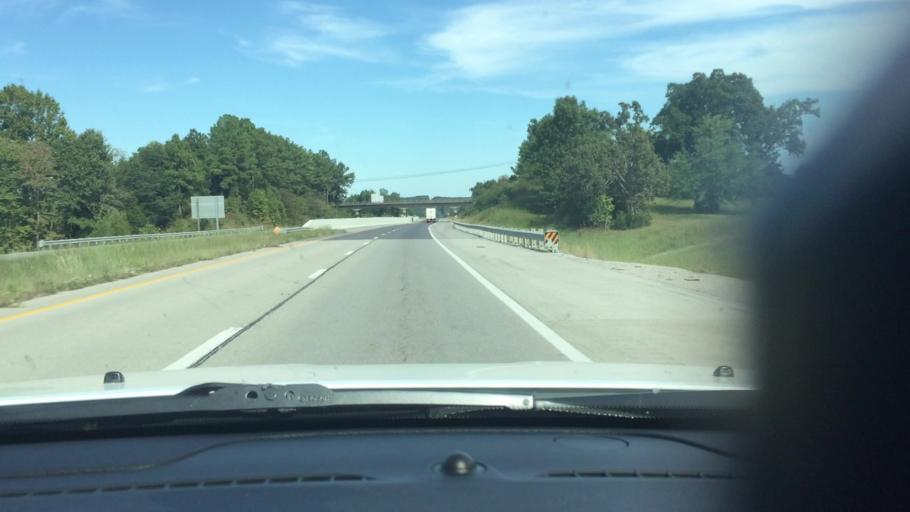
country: US
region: Kentucky
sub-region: Caldwell County
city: Princeton
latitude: 37.1316
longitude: -87.8743
